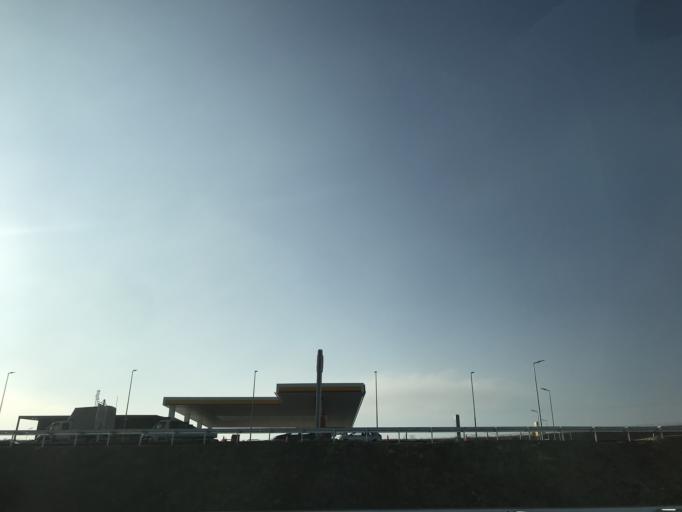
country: TR
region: Balikesir
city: Gobel
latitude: 40.0426
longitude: 28.2218
